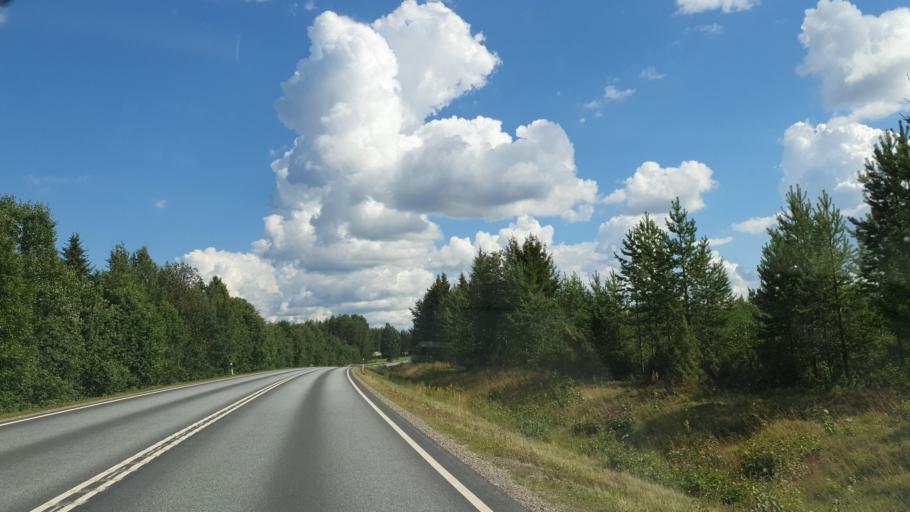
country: FI
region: Kainuu
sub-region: Kajaani
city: Sotkamo
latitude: 64.0991
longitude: 28.5319
